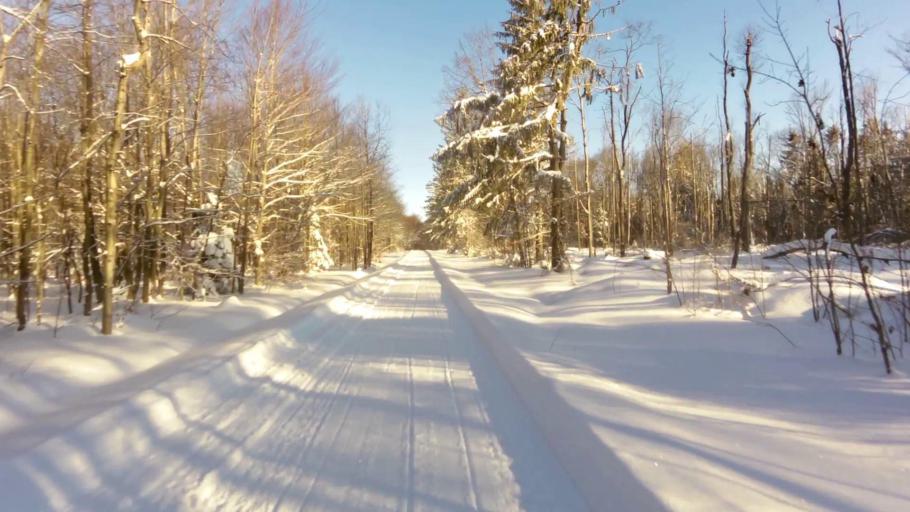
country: US
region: New York
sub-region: Chautauqua County
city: Falconer
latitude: 42.2453
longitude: -79.2131
